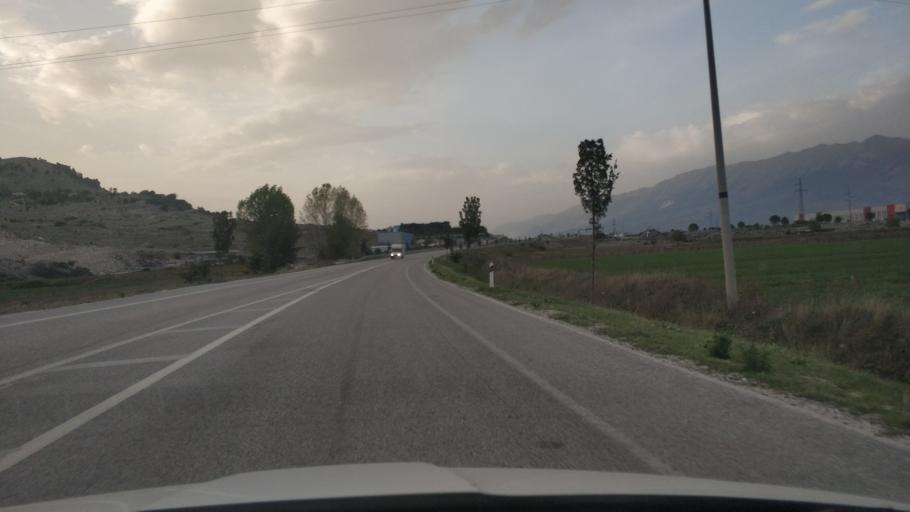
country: AL
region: Gjirokaster
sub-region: Rrethi i Gjirokastres
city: Libohove
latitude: 39.9693
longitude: 20.2375
